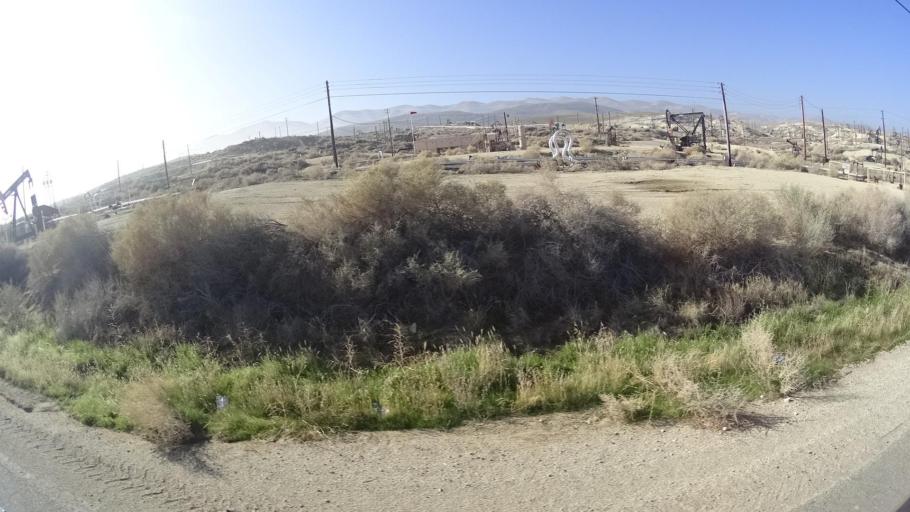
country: US
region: California
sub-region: Kern County
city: Taft Heights
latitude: 35.2053
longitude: -119.5974
